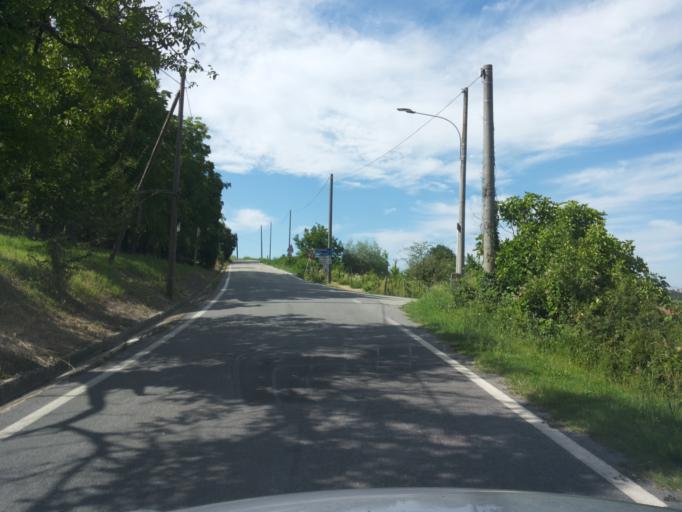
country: IT
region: Piedmont
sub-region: Provincia di Alessandria
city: Serralunga di Crea
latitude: 45.1004
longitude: 8.2868
